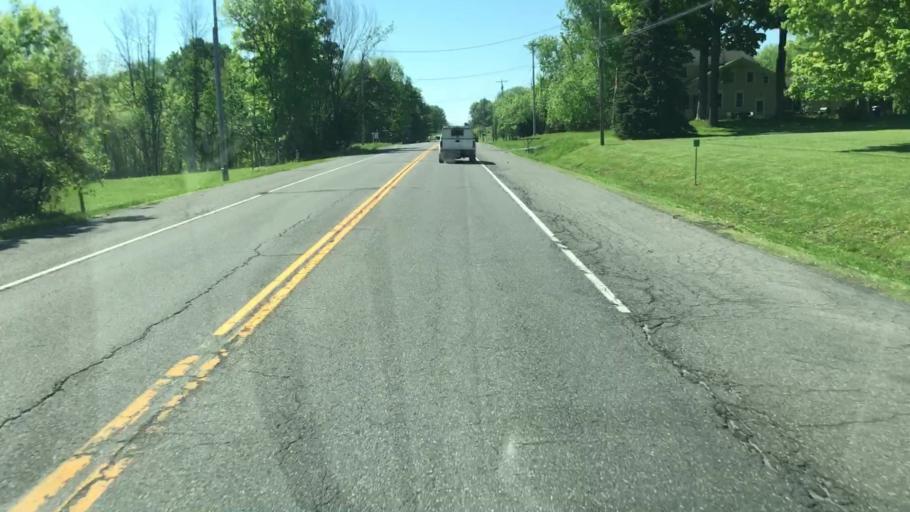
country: US
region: New York
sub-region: Onondaga County
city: Seneca Knolls
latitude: 43.1348
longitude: -76.2613
